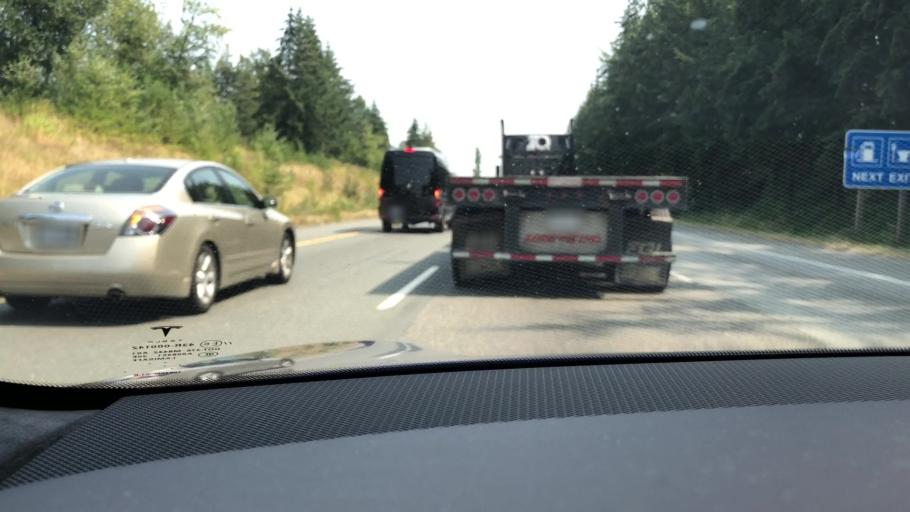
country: CA
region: British Columbia
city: Aldergrove
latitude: 49.1094
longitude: -122.5135
